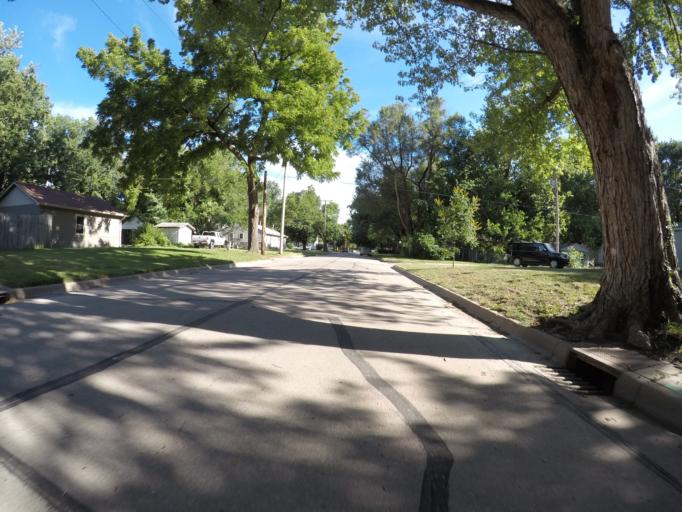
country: US
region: Kansas
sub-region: Riley County
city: Manhattan
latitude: 39.1906
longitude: -96.5650
